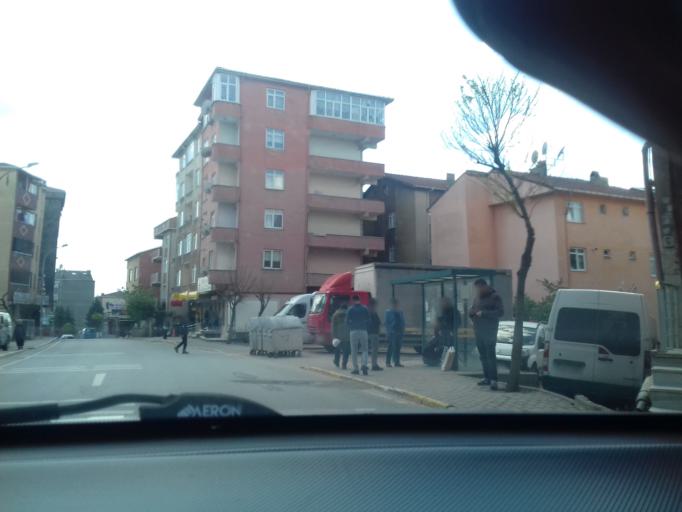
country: TR
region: Istanbul
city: Pendik
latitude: 40.8720
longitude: 29.2808
